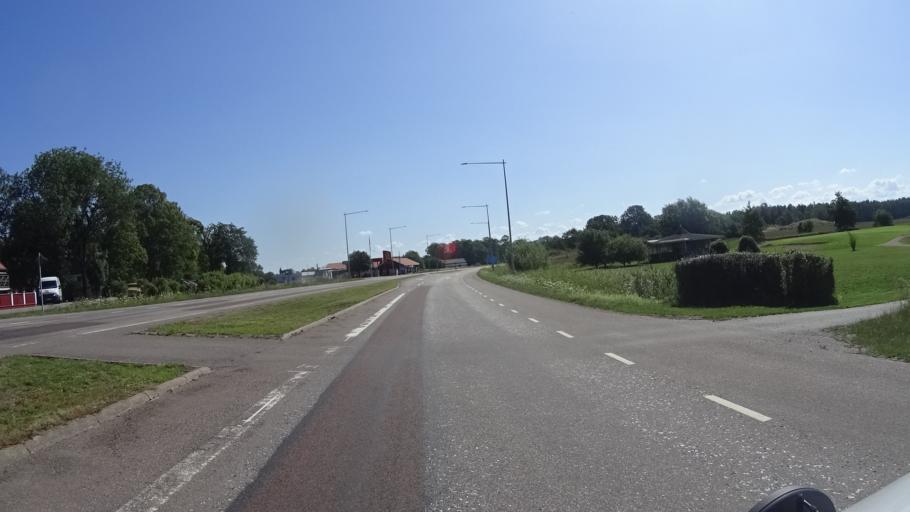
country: SE
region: OEstergoetland
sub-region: Vadstena Kommun
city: Herrestad
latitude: 58.3112
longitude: 14.9011
